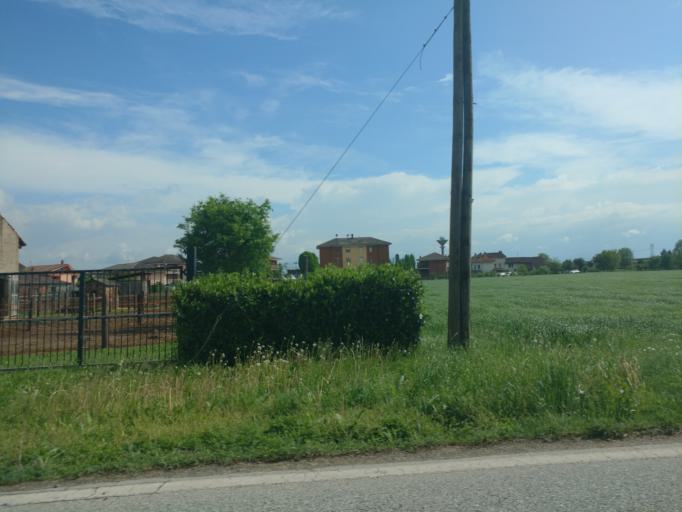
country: IT
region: Piedmont
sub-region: Provincia di Torino
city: Pancalieri
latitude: 44.8358
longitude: 7.5814
